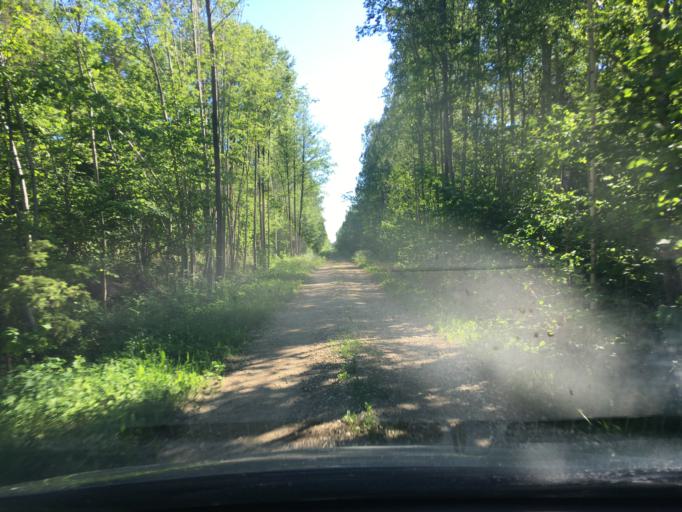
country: EE
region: Laeaene
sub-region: Lihula vald
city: Lihula
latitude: 58.6227
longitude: 23.7107
